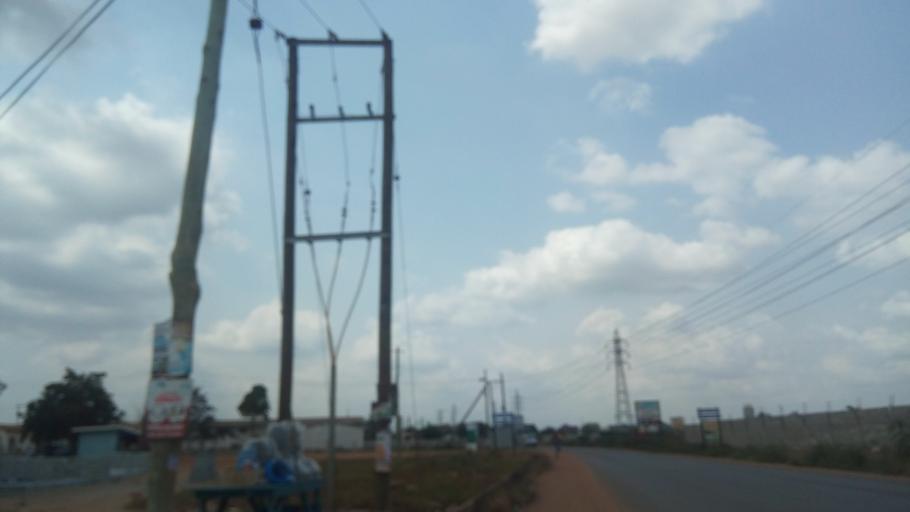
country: GH
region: Greater Accra
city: Tema
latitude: 5.7086
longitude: -0.0192
